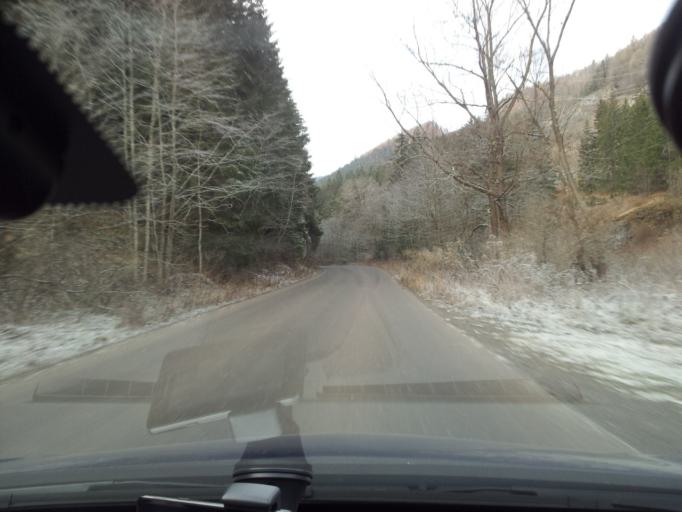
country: SK
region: Zilinsky
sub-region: Okres Liptovsky Mikulas
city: Hybe
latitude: 49.0122
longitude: 19.8818
